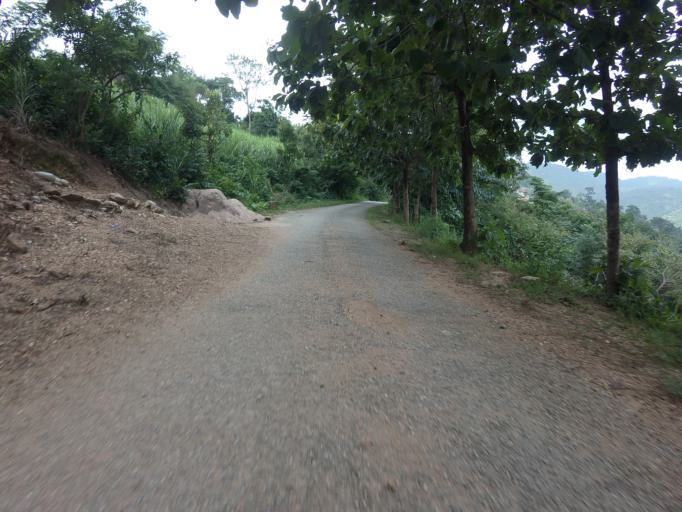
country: TG
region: Plateaux
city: Kpalime
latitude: 6.8890
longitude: 0.4514
